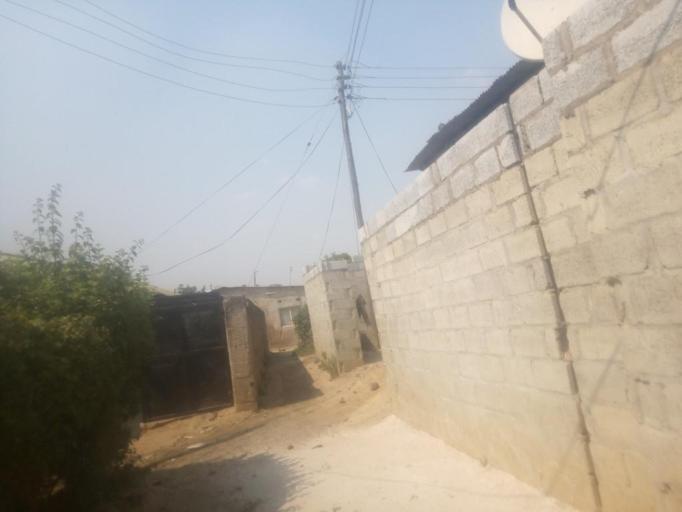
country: ZM
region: Lusaka
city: Lusaka
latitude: -15.4053
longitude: 28.3797
